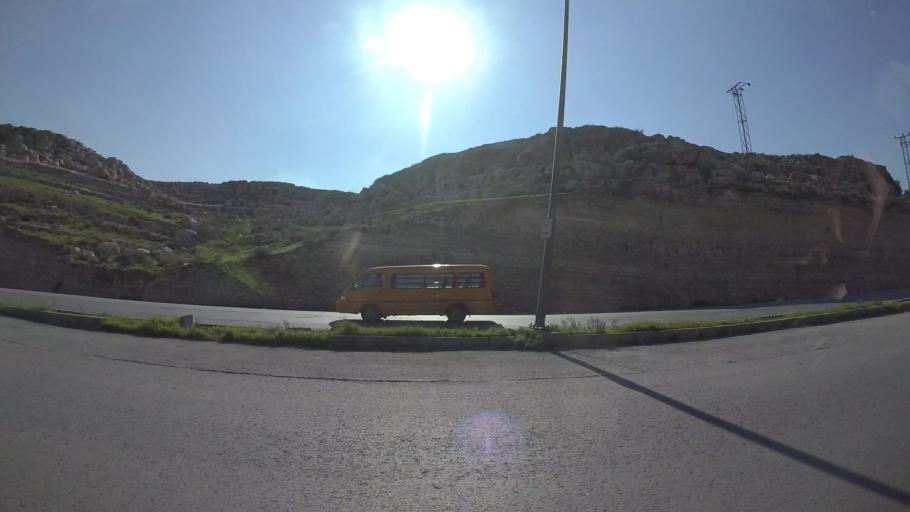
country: JO
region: Zarqa
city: Russeifa
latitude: 32.0183
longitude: 35.9900
